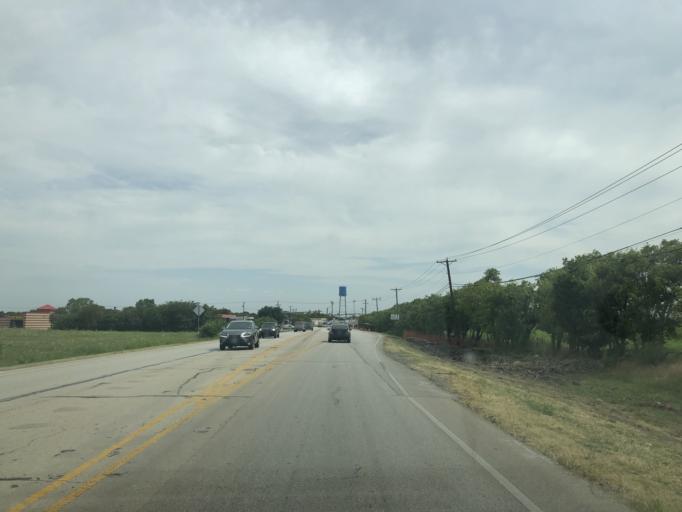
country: US
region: Texas
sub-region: Tarrant County
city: Blue Mound
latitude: 32.8661
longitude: -97.3424
